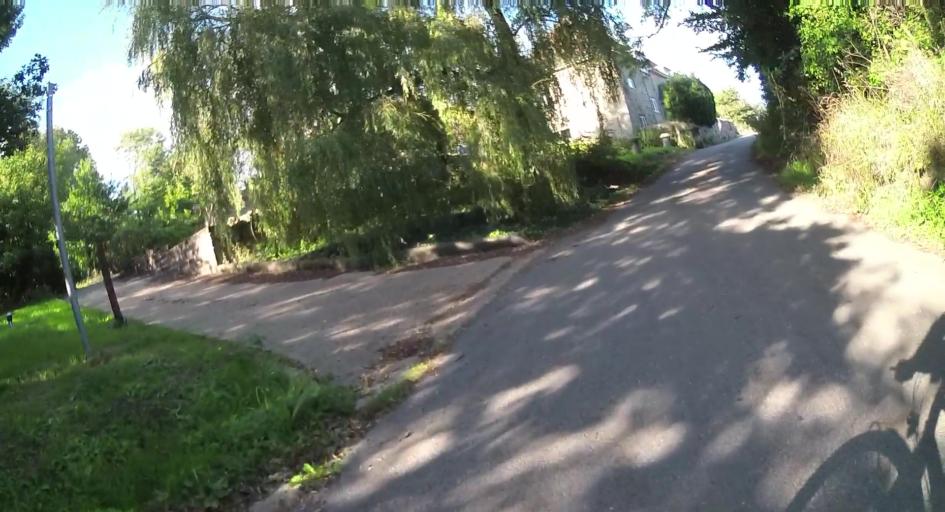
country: GB
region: England
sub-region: Isle of Wight
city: Chale
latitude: 50.6456
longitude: -1.3019
